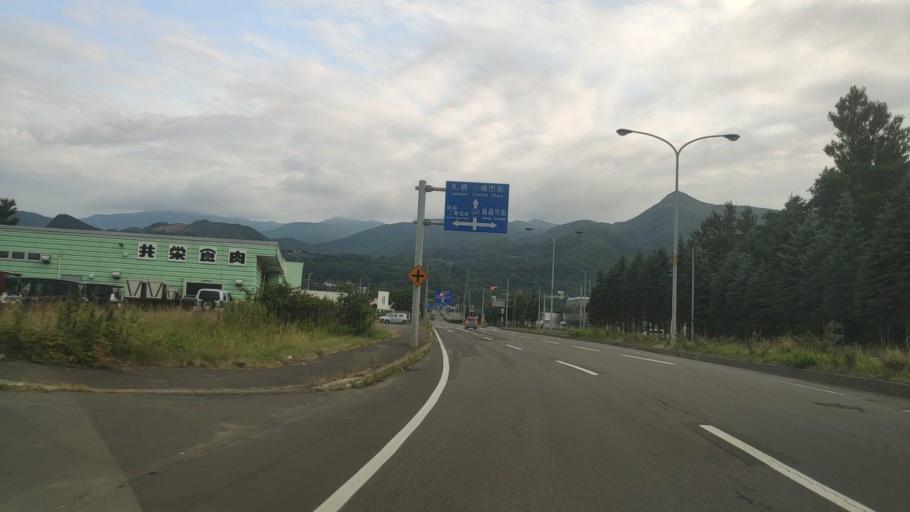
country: JP
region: Hokkaido
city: Otaru
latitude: 43.1425
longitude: 141.1795
